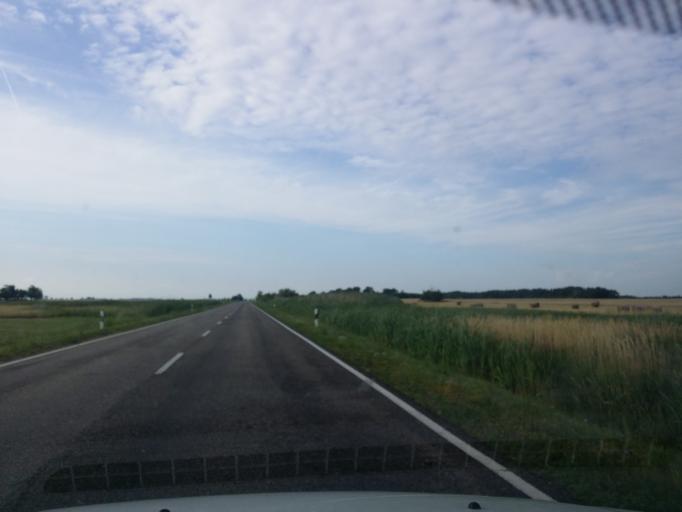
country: HU
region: Hajdu-Bihar
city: Egyek
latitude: 47.5740
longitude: 20.8578
